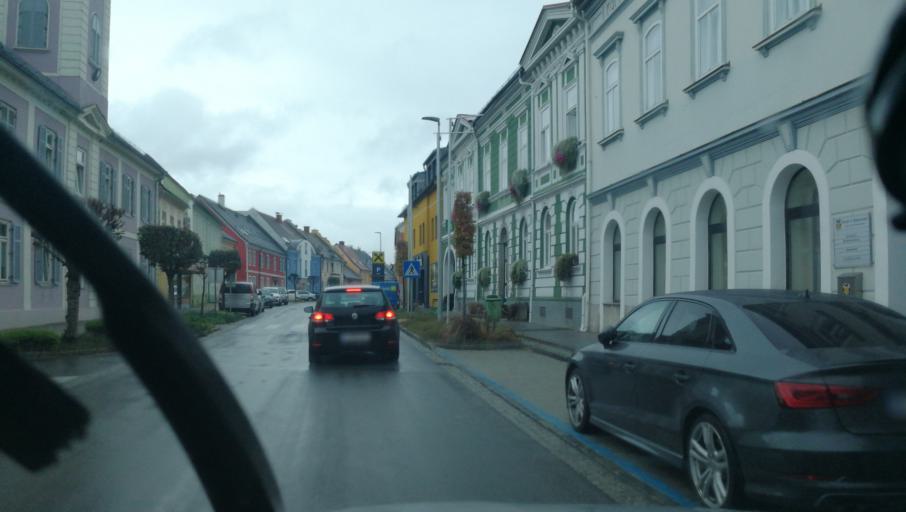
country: AT
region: Styria
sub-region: Politischer Bezirk Leibnitz
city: Strass in Steiermark
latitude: 46.7277
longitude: 15.6237
